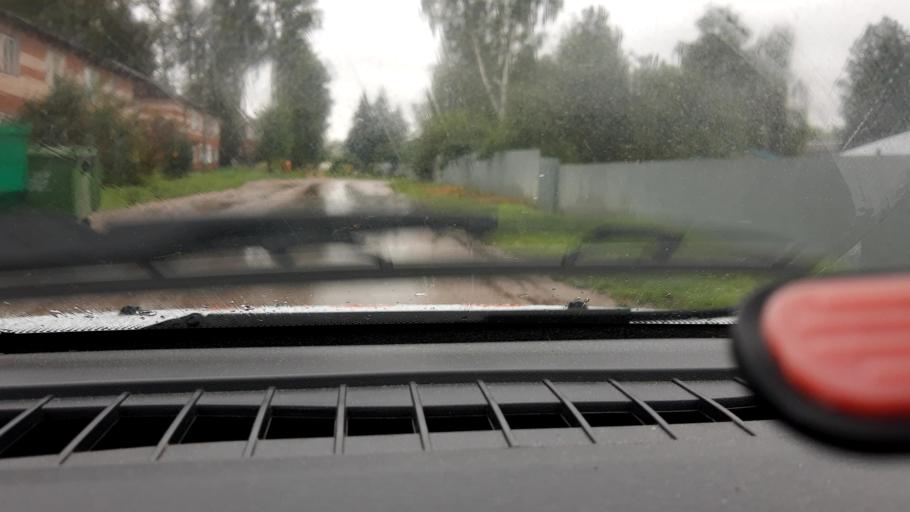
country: RU
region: Nizjnij Novgorod
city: Lyskovo
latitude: 56.0287
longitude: 45.0282
